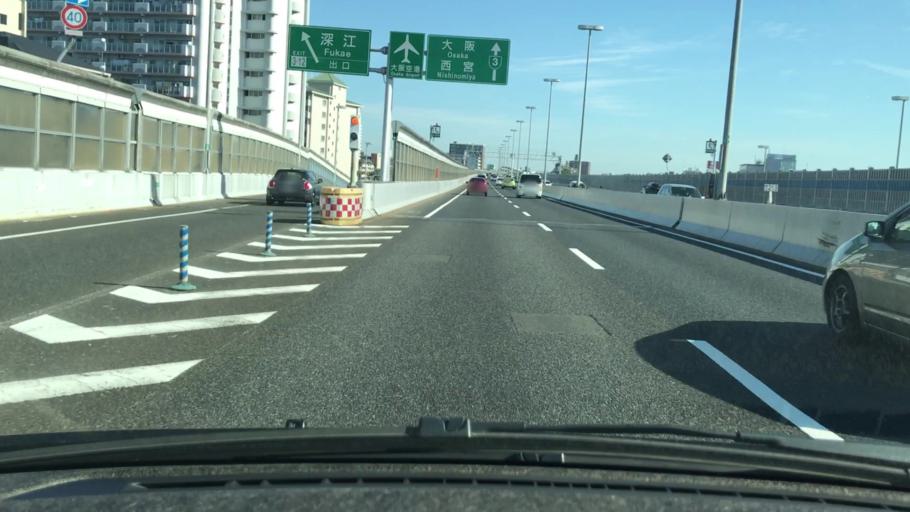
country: JP
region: Hyogo
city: Ashiya
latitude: 34.7179
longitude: 135.2857
